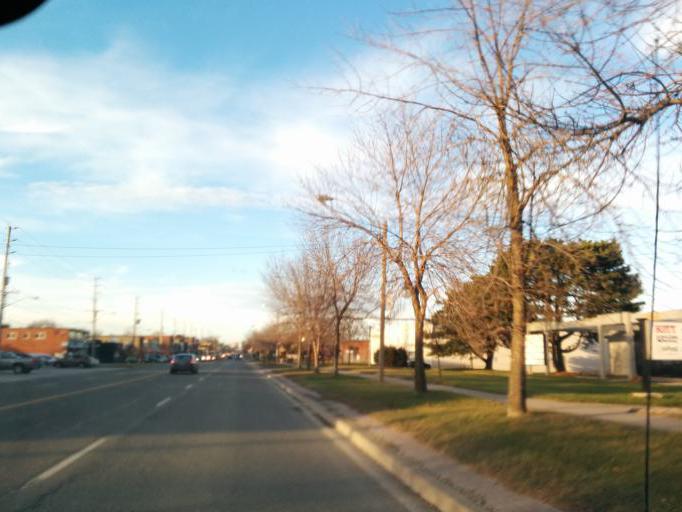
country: CA
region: Ontario
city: Etobicoke
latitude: 43.5974
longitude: -79.5432
